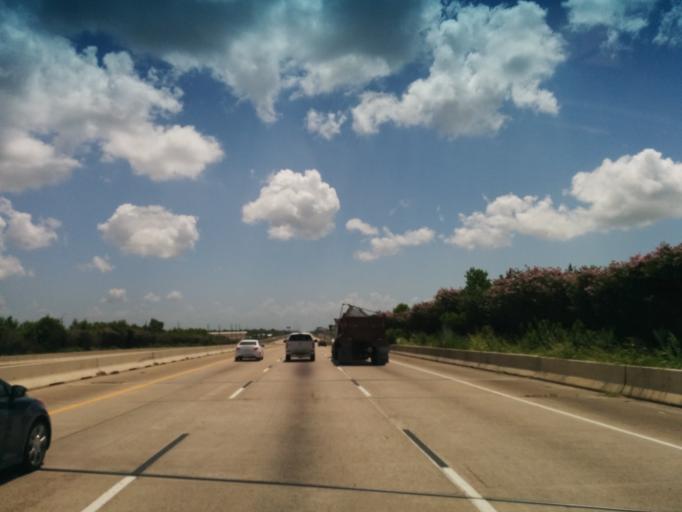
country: US
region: Texas
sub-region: Chambers County
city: Mont Belvieu
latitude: 29.8215
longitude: -94.8989
